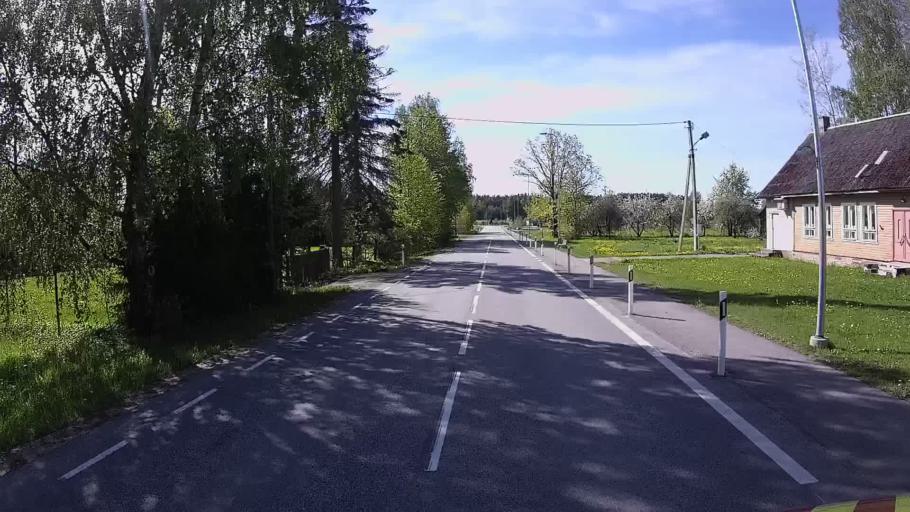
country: EE
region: Polvamaa
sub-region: Raepina vald
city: Rapina
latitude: 58.0024
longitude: 27.5435
